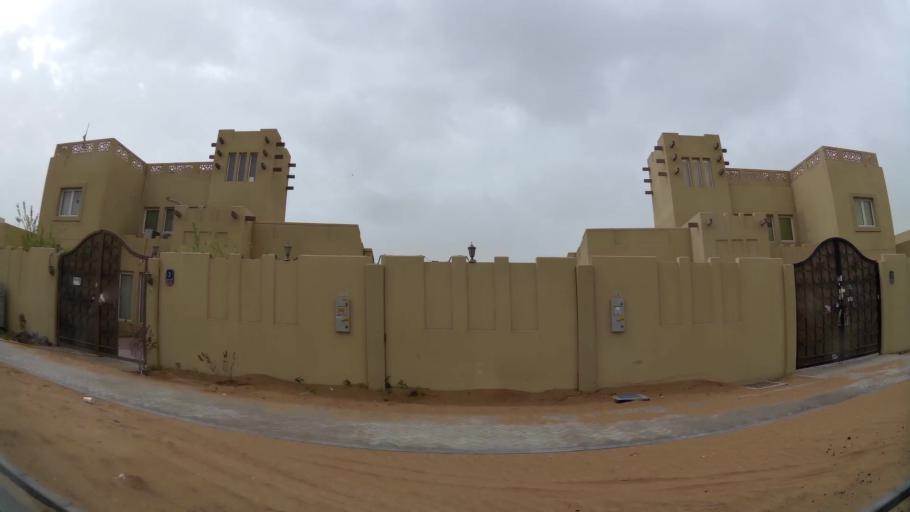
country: AE
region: Abu Dhabi
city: Abu Dhabi
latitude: 24.4534
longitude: 54.7208
